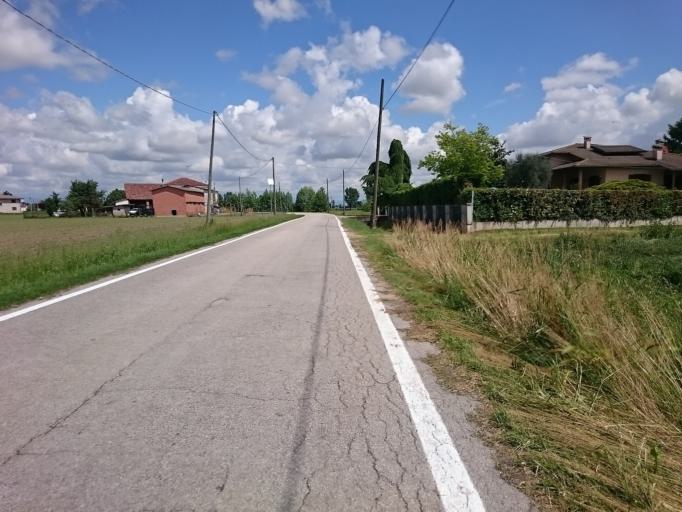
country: IT
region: Veneto
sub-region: Provincia di Padova
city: Campodoro
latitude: 45.4765
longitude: 11.7387
